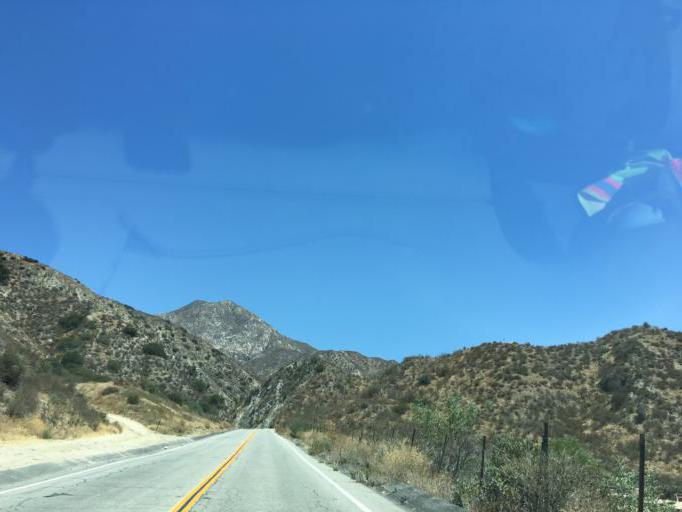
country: US
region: California
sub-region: Los Angeles County
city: La Crescenta-Montrose
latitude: 34.3017
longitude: -118.2666
